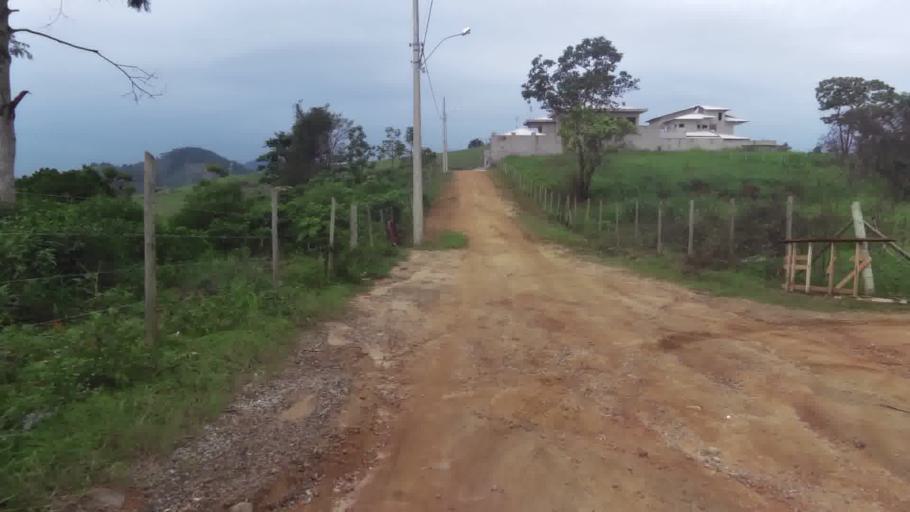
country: BR
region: Espirito Santo
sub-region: Iconha
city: Iconha
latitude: -20.7975
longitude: -40.8093
